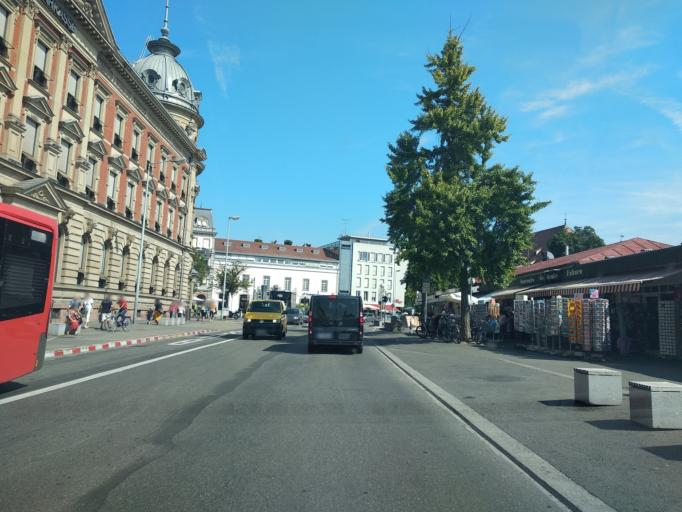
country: DE
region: Baden-Wuerttemberg
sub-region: Freiburg Region
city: Konstanz
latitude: 47.6603
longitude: 9.1774
